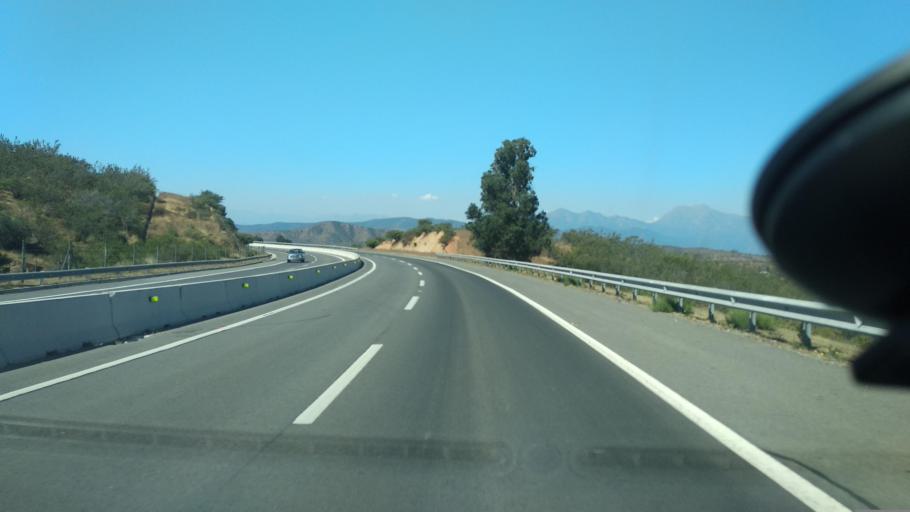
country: CL
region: Valparaiso
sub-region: Provincia de Marga Marga
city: Villa Alemana
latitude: -33.0434
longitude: -71.3201
